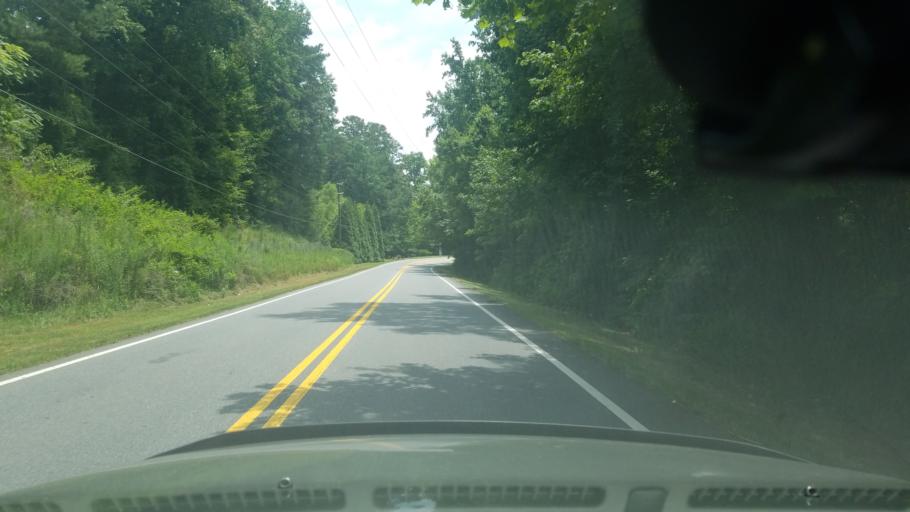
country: US
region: Georgia
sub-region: Fulton County
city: Milton
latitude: 34.1638
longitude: -84.2713
